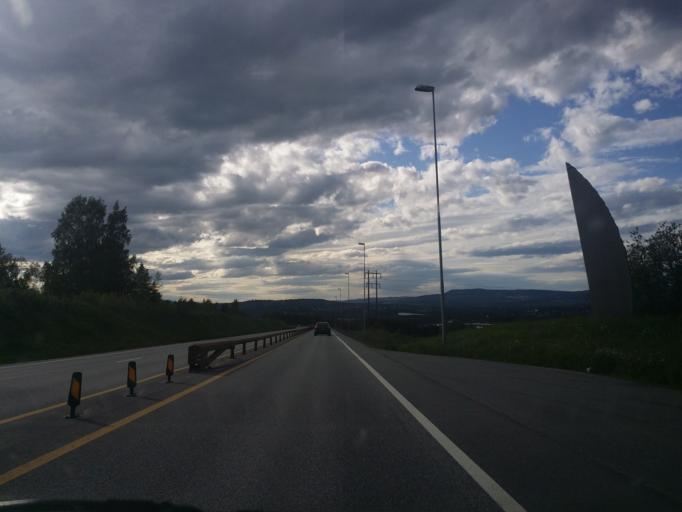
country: NO
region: Hedmark
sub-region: Stange
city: Stange
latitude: 60.7765
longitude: 11.1515
